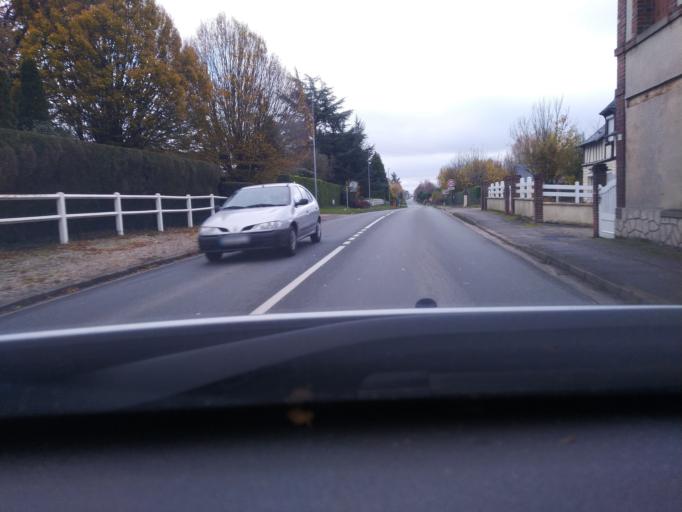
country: FR
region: Haute-Normandie
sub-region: Departement de la Seine-Maritime
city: La Vaupaliere
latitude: 49.4894
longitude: 1.0027
